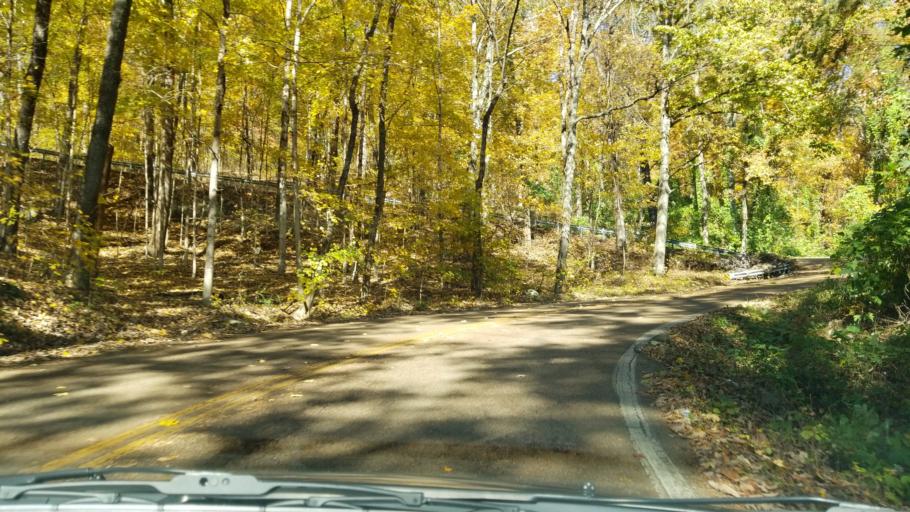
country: US
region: Tennessee
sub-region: Hamilton County
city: Falling Water
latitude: 35.2071
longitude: -85.2592
